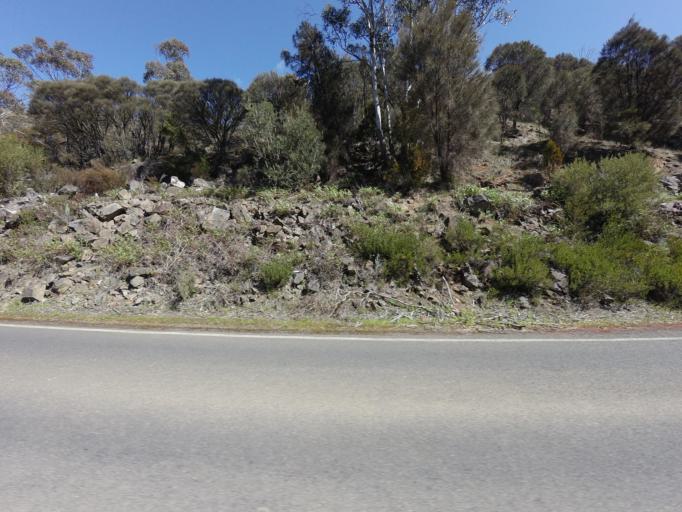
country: AU
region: Tasmania
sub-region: Derwent Valley
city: New Norfolk
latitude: -42.6824
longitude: 146.7677
